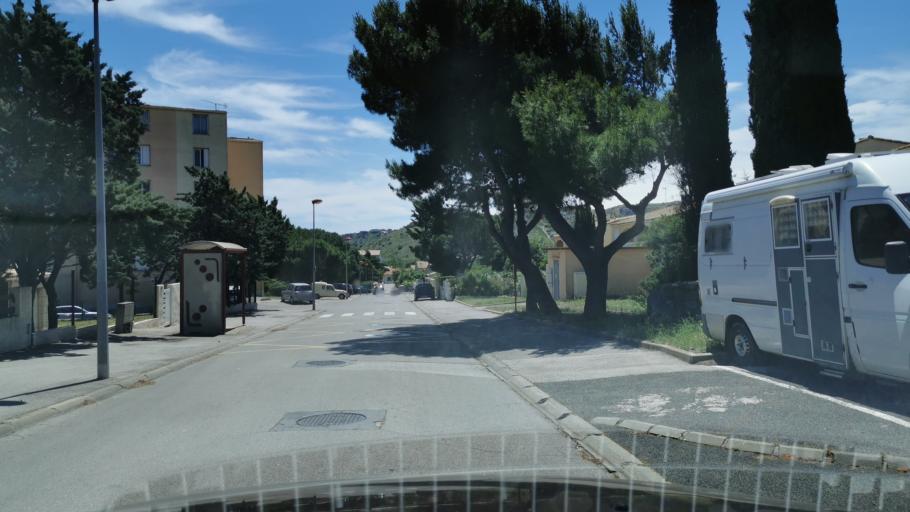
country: FR
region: Languedoc-Roussillon
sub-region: Departement de l'Aude
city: Narbonne
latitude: 43.1841
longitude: 2.9713
